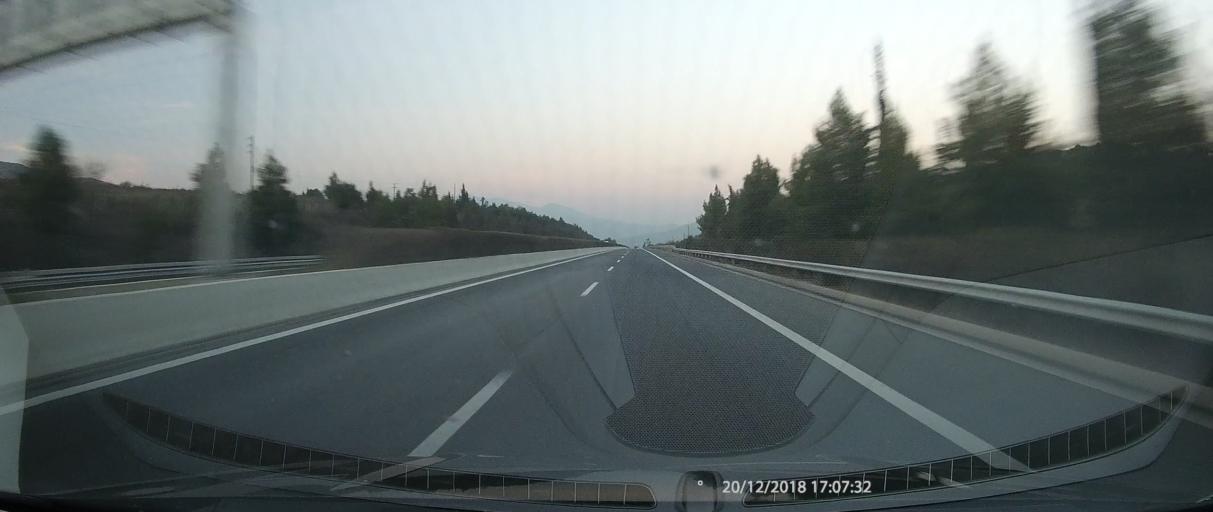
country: GR
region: Thessaly
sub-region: Nomos Larisis
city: Makrychori
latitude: 39.7799
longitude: 22.4893
